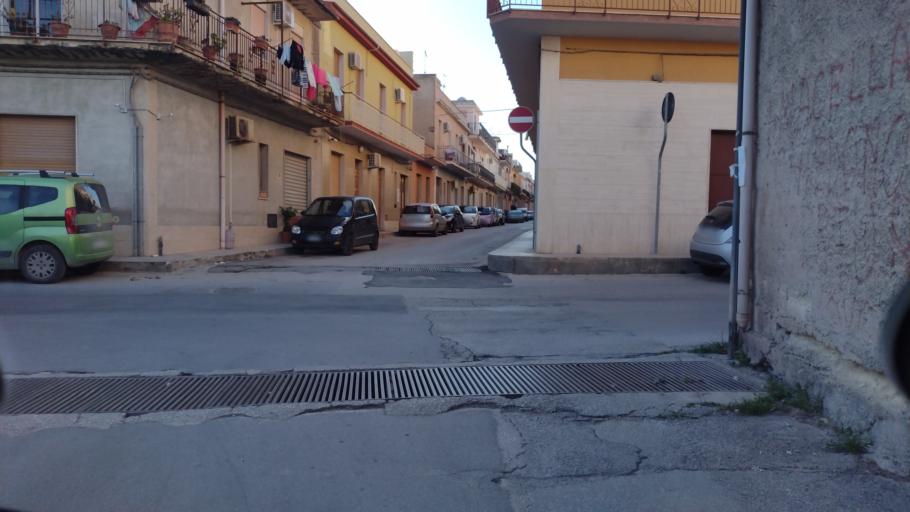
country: IT
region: Sicily
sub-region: Provincia di Siracusa
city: Avola
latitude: 36.9023
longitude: 15.1361
